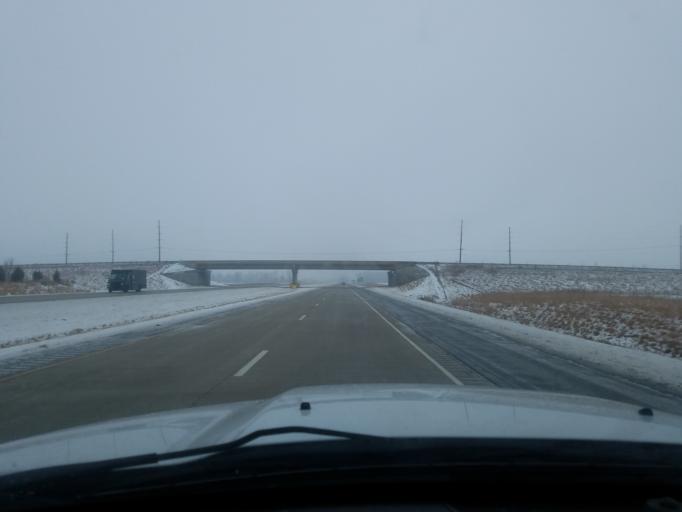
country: US
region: Indiana
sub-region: Howard County
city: Indian Heights
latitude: 40.4471
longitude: -86.0770
